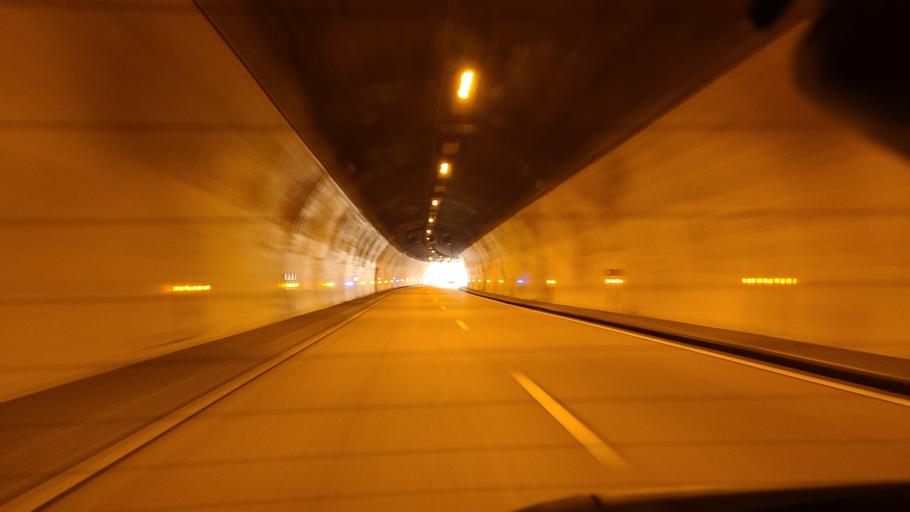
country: FR
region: Provence-Alpes-Cote d'Azur
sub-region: Departement des Alpes-Maritimes
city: Gorbio
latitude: 43.7733
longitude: 7.4499
